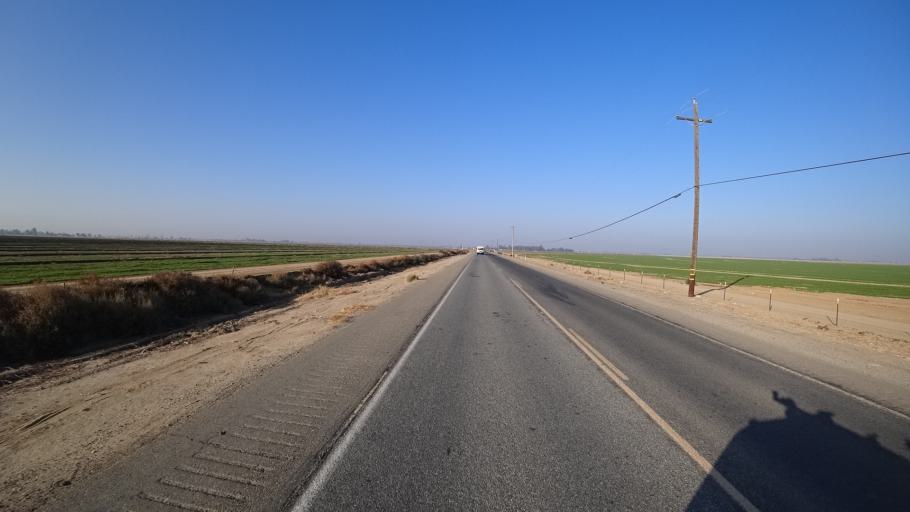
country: US
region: California
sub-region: Kern County
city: Lamont
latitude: 35.2669
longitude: -118.9528
